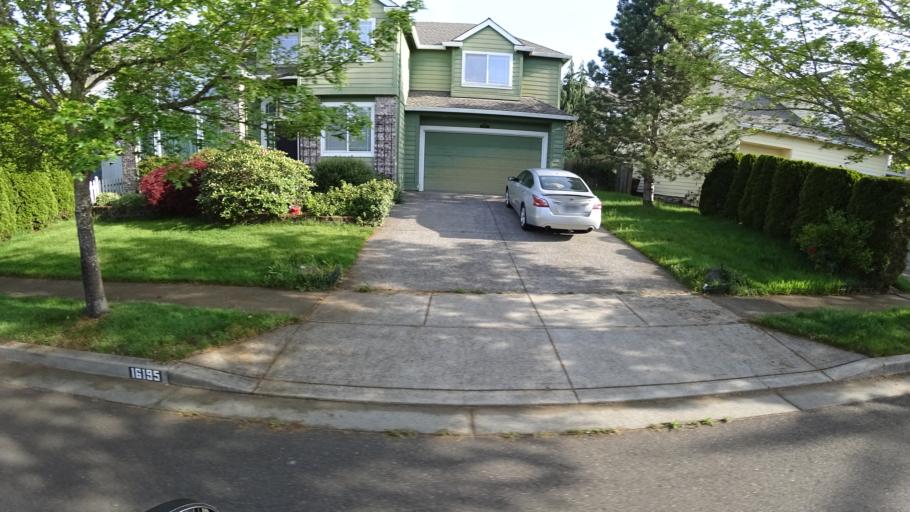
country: US
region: Oregon
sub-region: Washington County
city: King City
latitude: 45.4327
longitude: -122.8433
